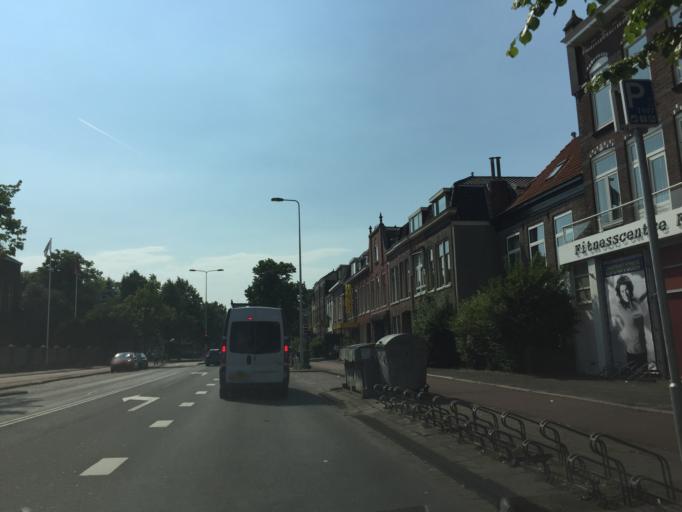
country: NL
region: South Holland
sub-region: Gemeente Leiden
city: Leiden
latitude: 52.1553
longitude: 4.5089
